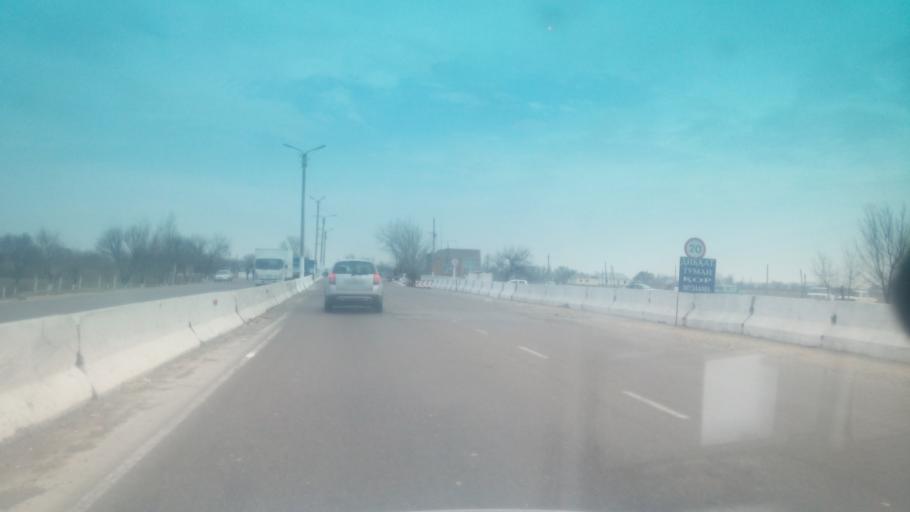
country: KZ
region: Ongtustik Qazaqstan
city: Myrzakent
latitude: 40.5037
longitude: 68.5217
